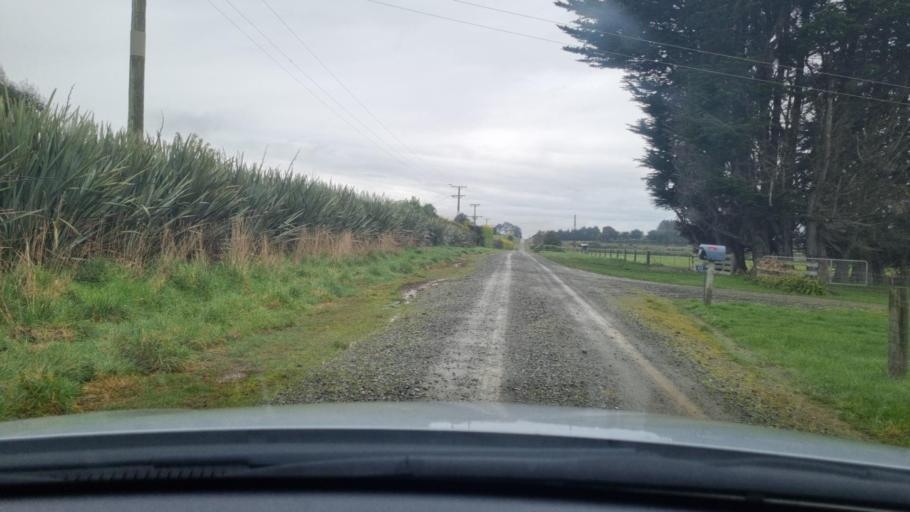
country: NZ
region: Southland
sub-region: Invercargill City
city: Invercargill
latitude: -46.3222
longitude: 168.3310
